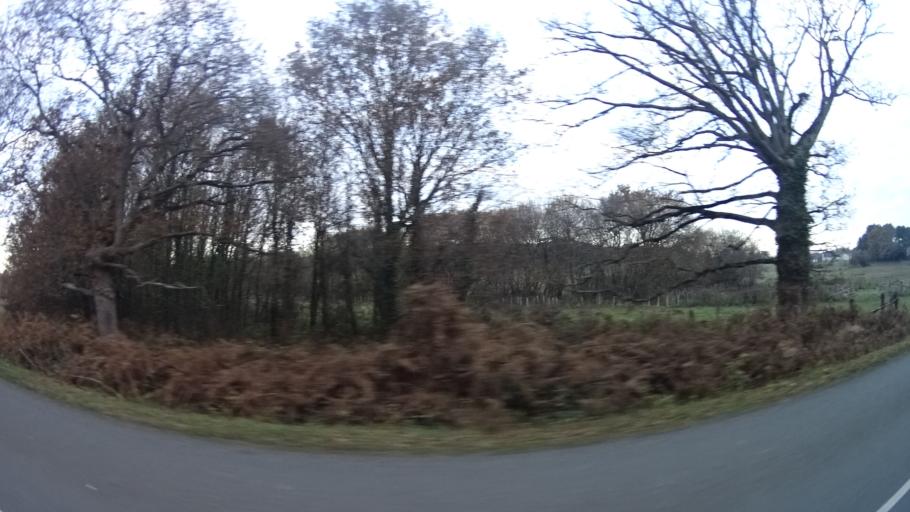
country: FR
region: Brittany
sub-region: Departement d'Ille-et-Vilaine
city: Langon
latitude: 47.6903
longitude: -1.8730
